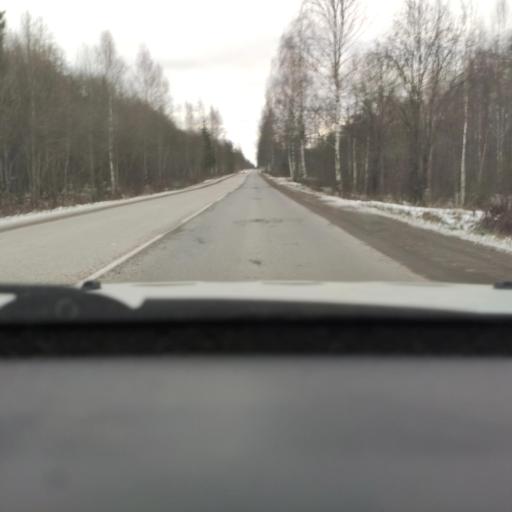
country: RU
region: Perm
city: Polazna
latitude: 58.1062
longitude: 56.4182
